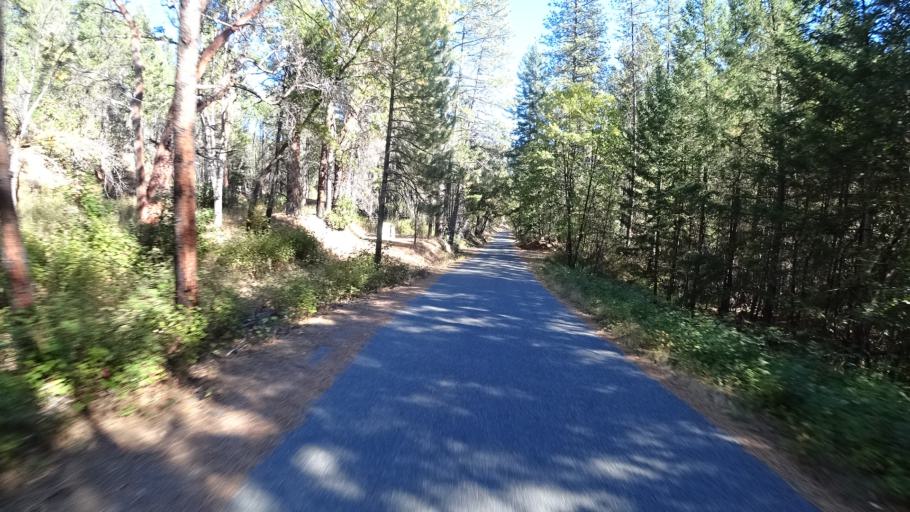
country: US
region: California
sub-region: Siskiyou County
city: Happy Camp
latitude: 41.3159
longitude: -123.1906
